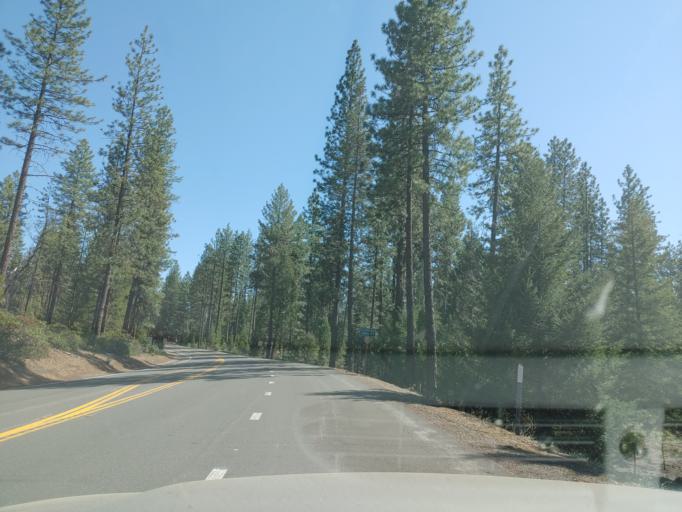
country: US
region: California
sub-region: Shasta County
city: Burney
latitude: 41.0107
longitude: -121.6490
